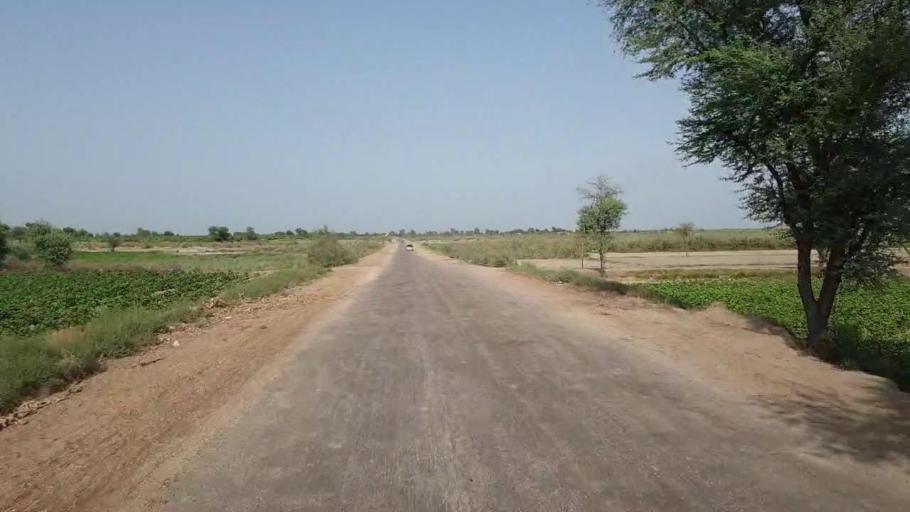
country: PK
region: Sindh
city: Sakrand
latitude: 26.2846
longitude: 68.2385
